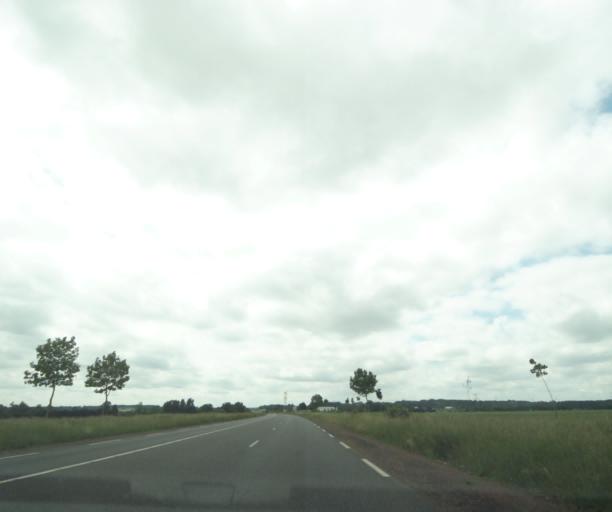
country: FR
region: Poitou-Charentes
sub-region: Departement des Deux-Sevres
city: Saint-Varent
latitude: 46.8387
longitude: -0.2083
